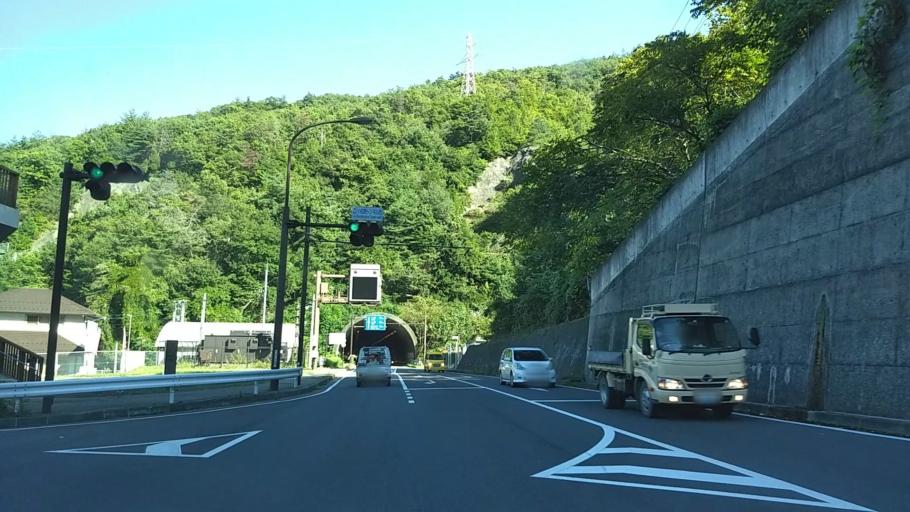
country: JP
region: Nagano
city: Nagano-shi
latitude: 36.6188
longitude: 138.1232
